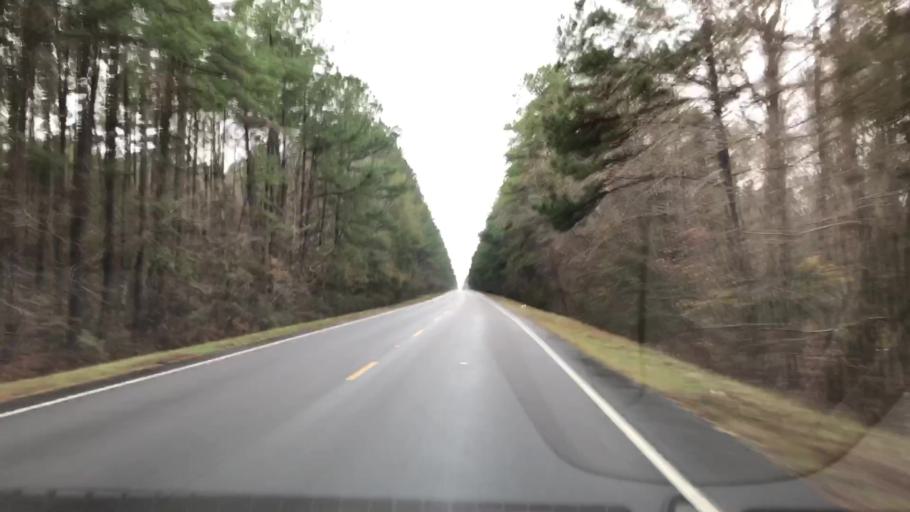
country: US
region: South Carolina
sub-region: Berkeley County
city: Saint Stephen
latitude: 33.2901
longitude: -79.7963
